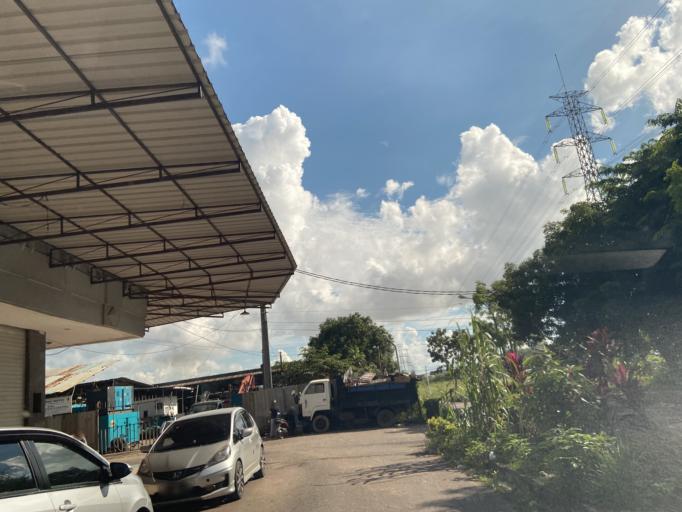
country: SG
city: Singapore
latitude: 1.1257
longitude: 104.0259
